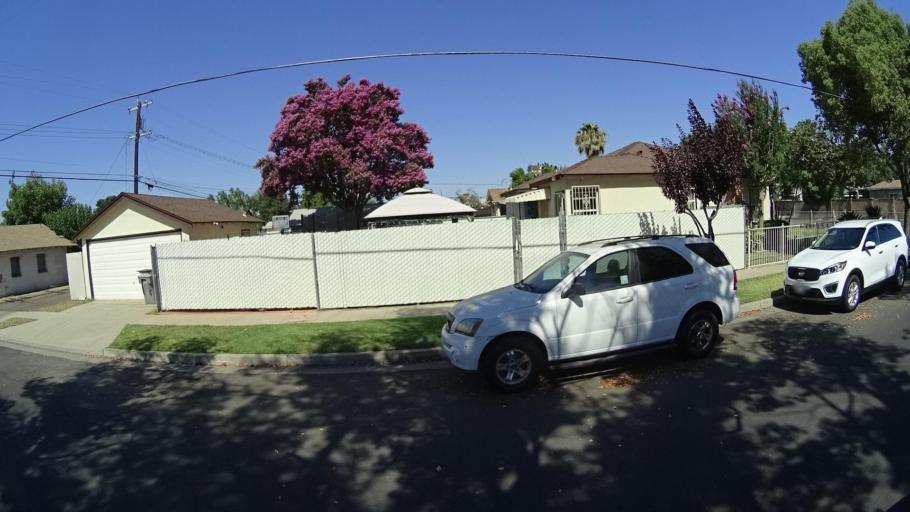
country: US
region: California
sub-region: Fresno County
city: Fresno
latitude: 36.7274
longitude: -119.7614
